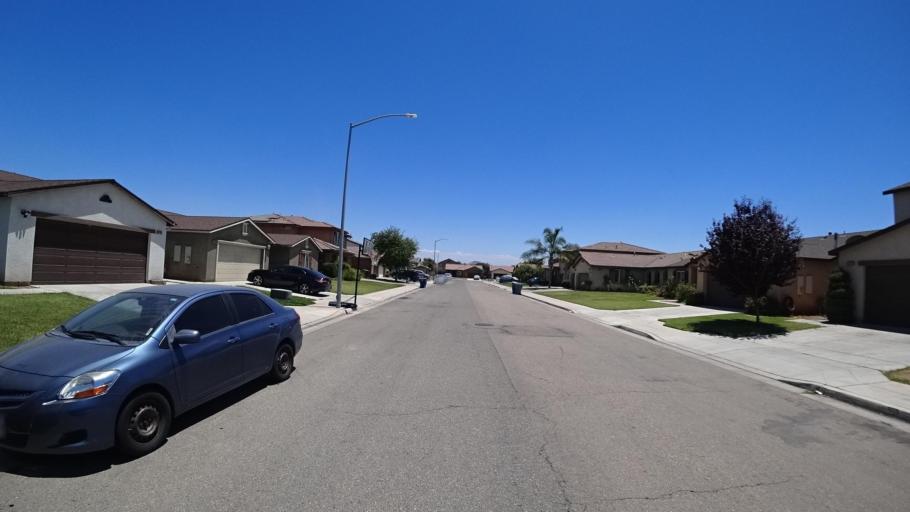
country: US
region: California
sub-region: Fresno County
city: Sunnyside
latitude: 36.7271
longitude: -119.6684
